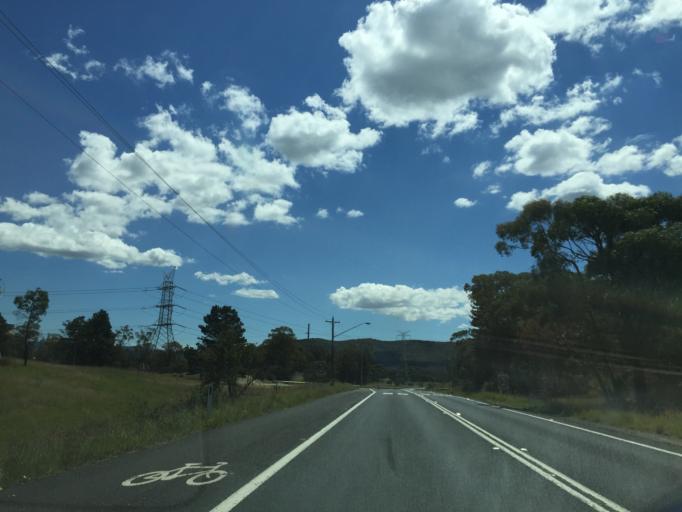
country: AU
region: New South Wales
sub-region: Lithgow
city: Lithgow
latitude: -33.3992
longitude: 150.0887
